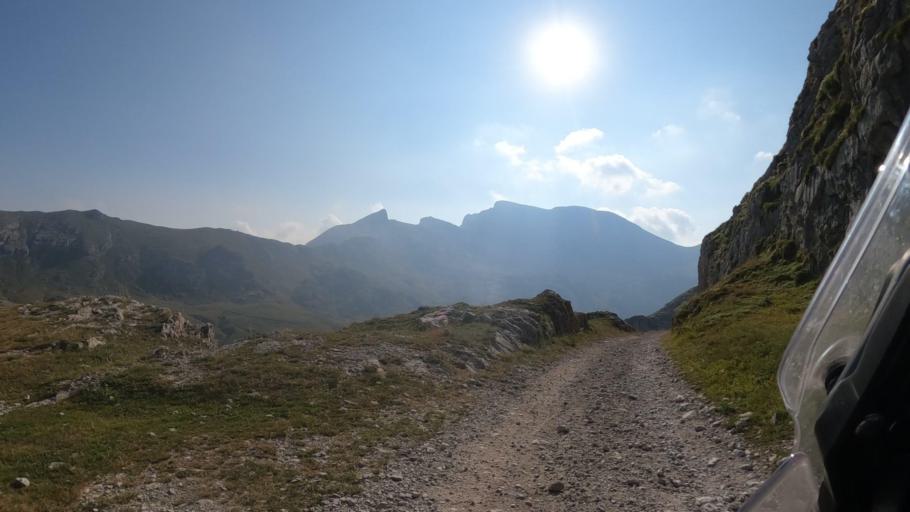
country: IT
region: Piedmont
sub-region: Provincia di Cuneo
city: Limone Piemonte
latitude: 44.1698
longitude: 7.6545
